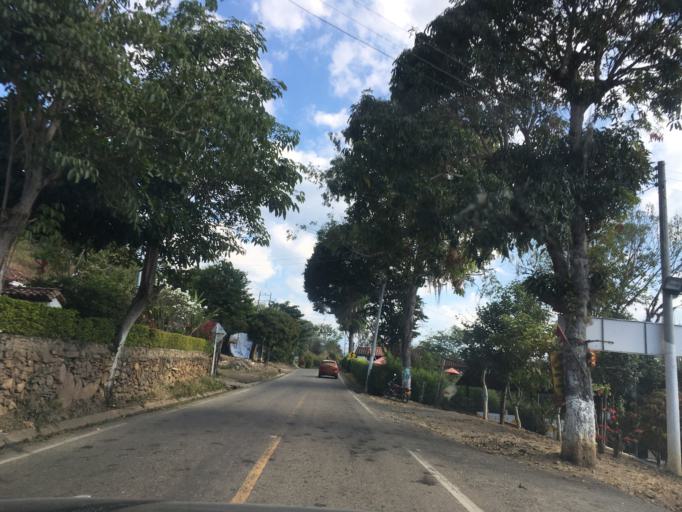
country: CO
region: Santander
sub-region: San Gil
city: San Gil
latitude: 6.5759
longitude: -73.1527
